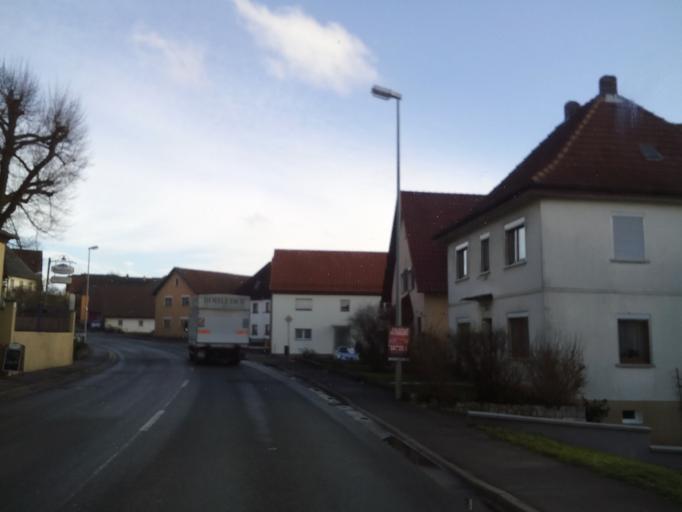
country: DE
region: Bavaria
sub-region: Upper Franconia
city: Mainleus
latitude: 50.1224
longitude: 11.3176
